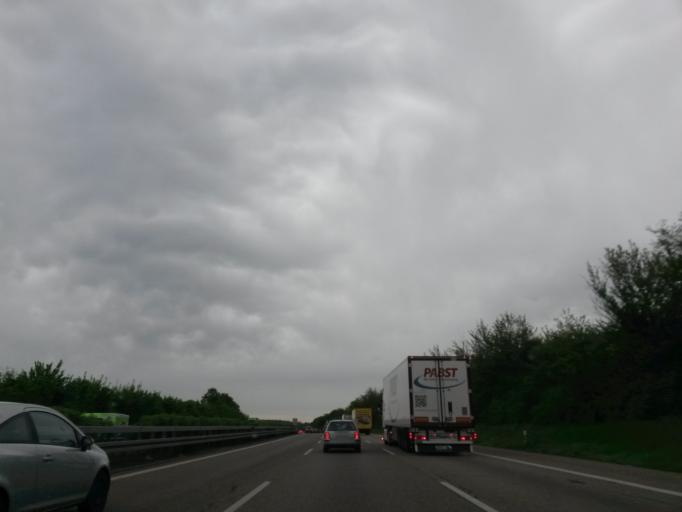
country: DE
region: Baden-Wuerttemberg
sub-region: Regierungsbezirk Stuttgart
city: Abstatt
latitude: 49.0664
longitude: 9.2773
